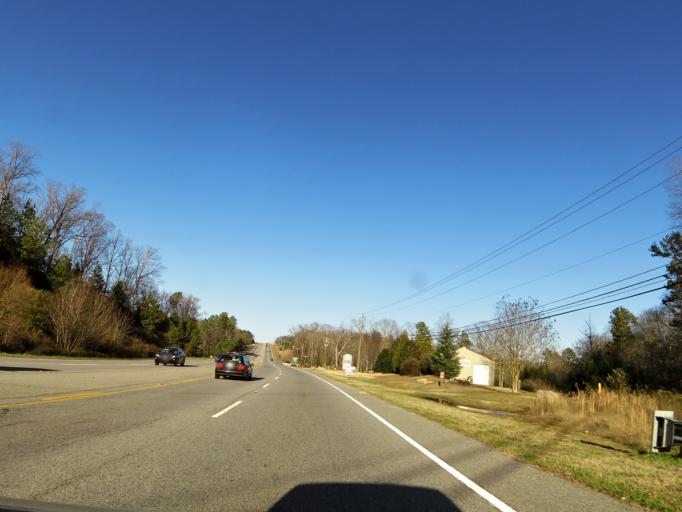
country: US
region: South Carolina
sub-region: Spartanburg County
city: Fairforest
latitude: 34.8927
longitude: -82.0417
